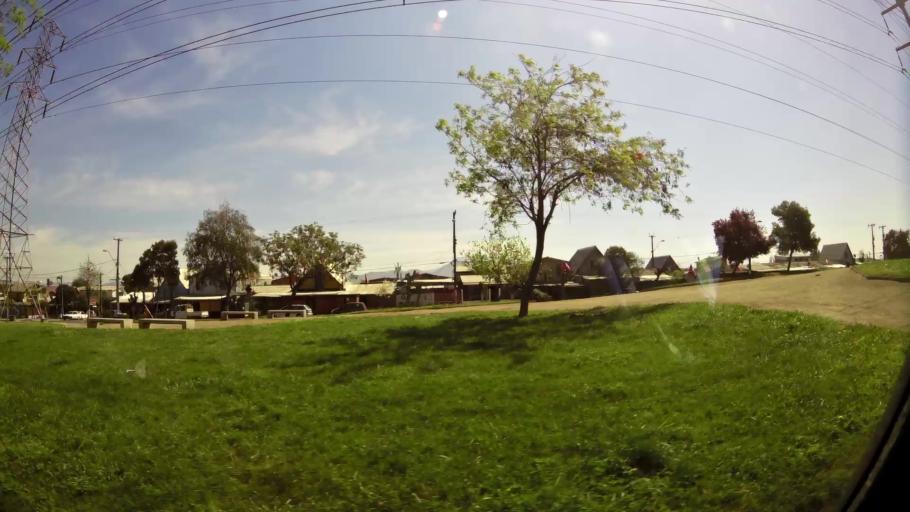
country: CL
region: Santiago Metropolitan
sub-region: Provincia de Santiago
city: Lo Prado
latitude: -33.5014
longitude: -70.7338
